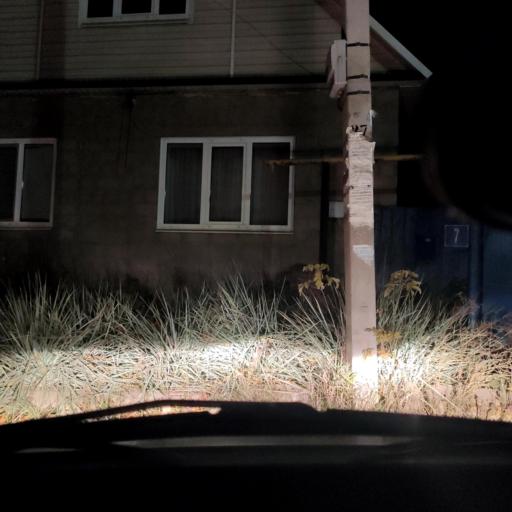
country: RU
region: Bashkortostan
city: Ufa
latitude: 54.7272
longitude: 56.0074
